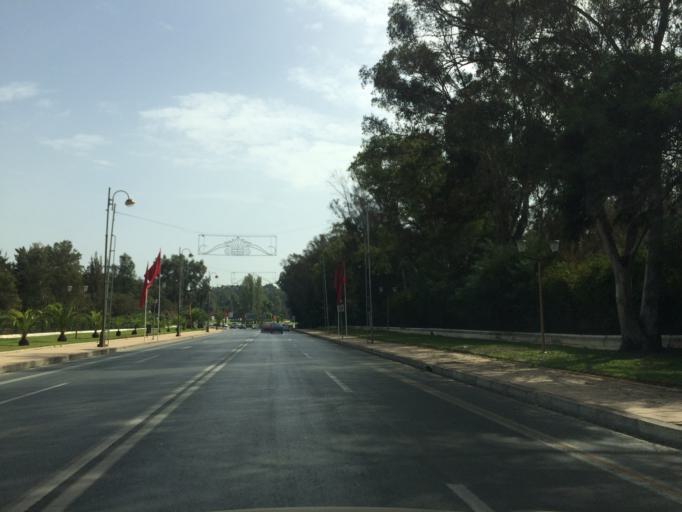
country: MA
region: Rabat-Sale-Zemmour-Zaer
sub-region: Rabat
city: Rabat
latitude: 33.9961
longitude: -6.8372
